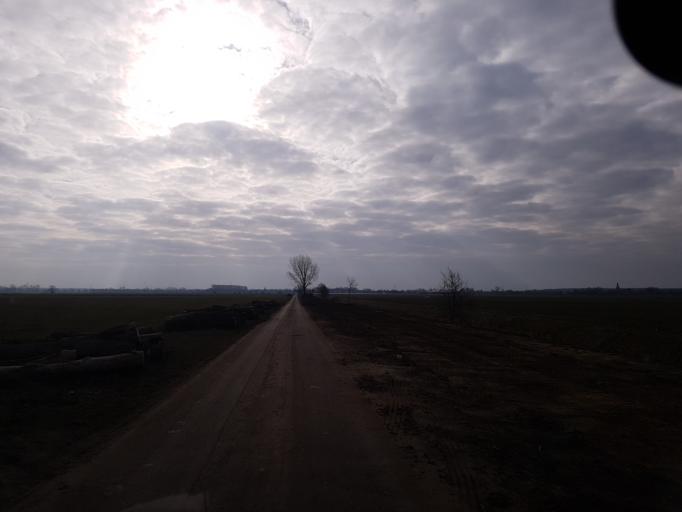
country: DE
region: Brandenburg
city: Doberlug-Kirchhain
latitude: 51.6677
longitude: 13.5392
